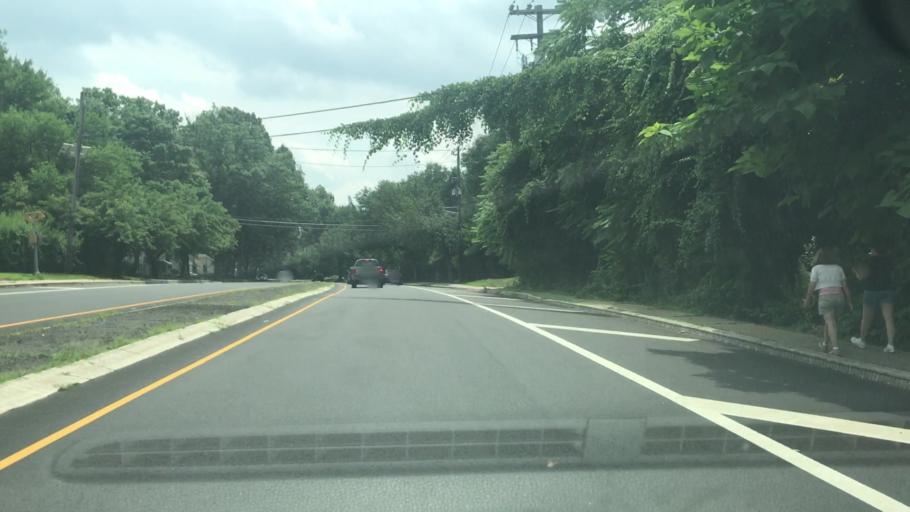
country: US
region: New Jersey
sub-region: Union County
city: Clark
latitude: 40.6400
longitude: -74.3055
